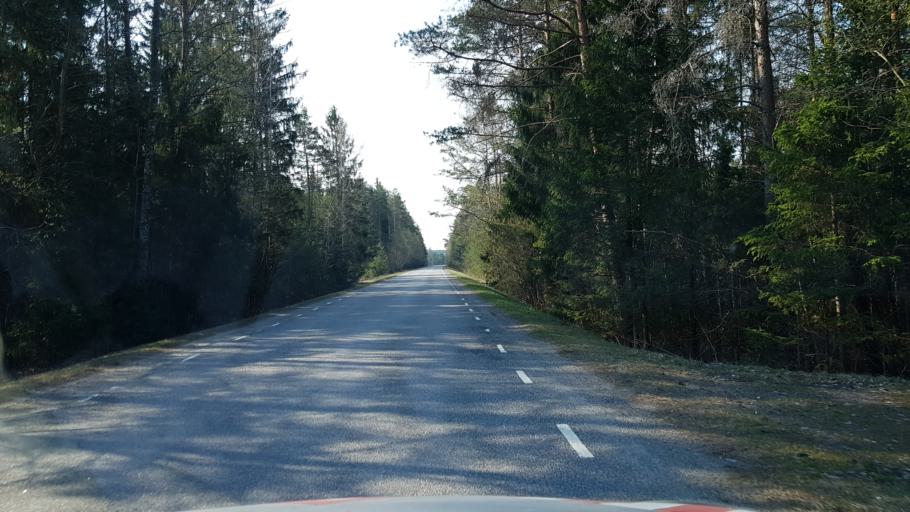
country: EE
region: Raplamaa
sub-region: Kohila vald
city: Kohila
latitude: 59.1928
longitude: 24.6626
